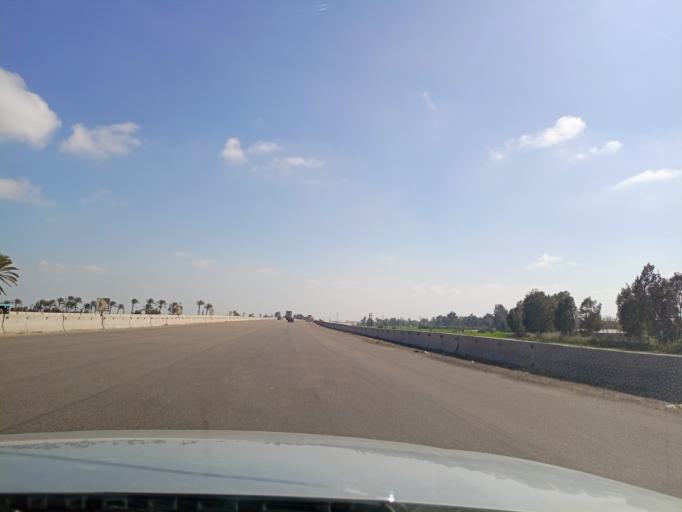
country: EG
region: Eastern Province
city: Mashtul as Suq
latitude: 30.4651
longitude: 31.3121
